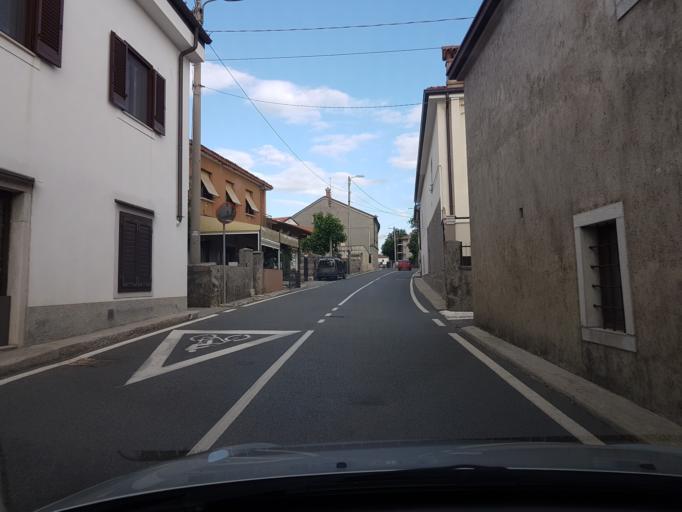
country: IT
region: Friuli Venezia Giulia
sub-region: Provincia di Trieste
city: Villa Opicina
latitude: 45.6736
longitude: 13.8233
